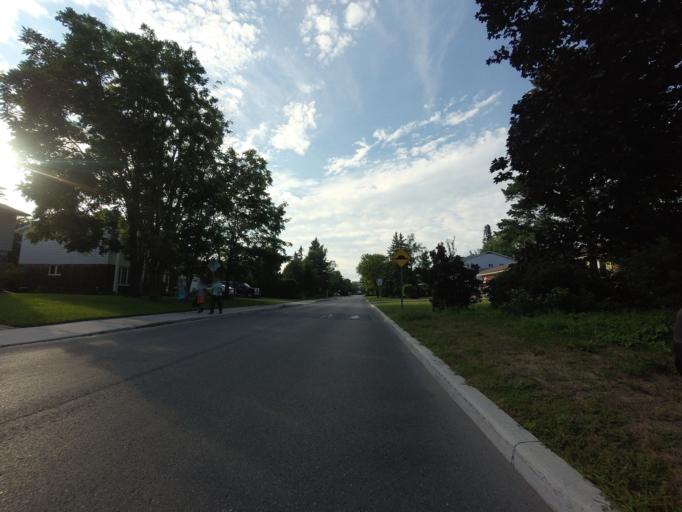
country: CA
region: Ontario
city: Bells Corners
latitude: 45.2817
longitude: -75.7655
